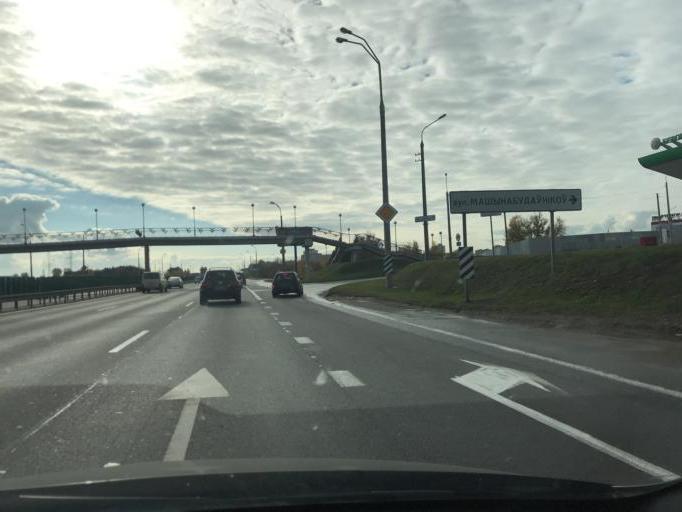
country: BY
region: Minsk
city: Vyaliki Trastsyanets
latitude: 53.8496
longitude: 27.6716
